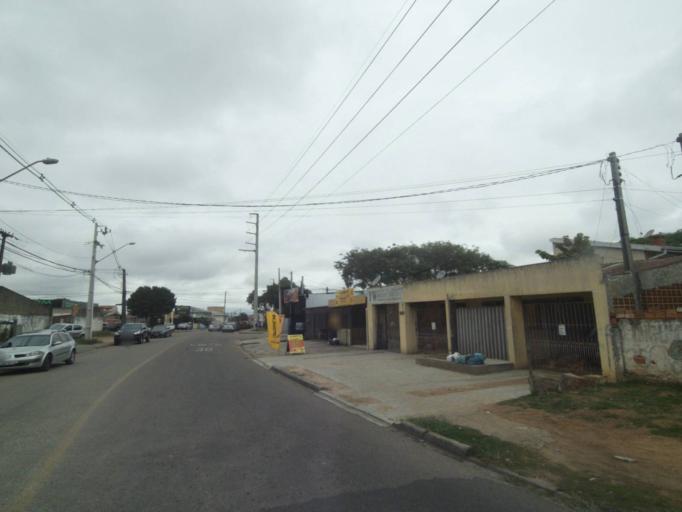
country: BR
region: Parana
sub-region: Sao Jose Dos Pinhais
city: Sao Jose dos Pinhais
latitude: -25.5435
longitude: -49.2780
